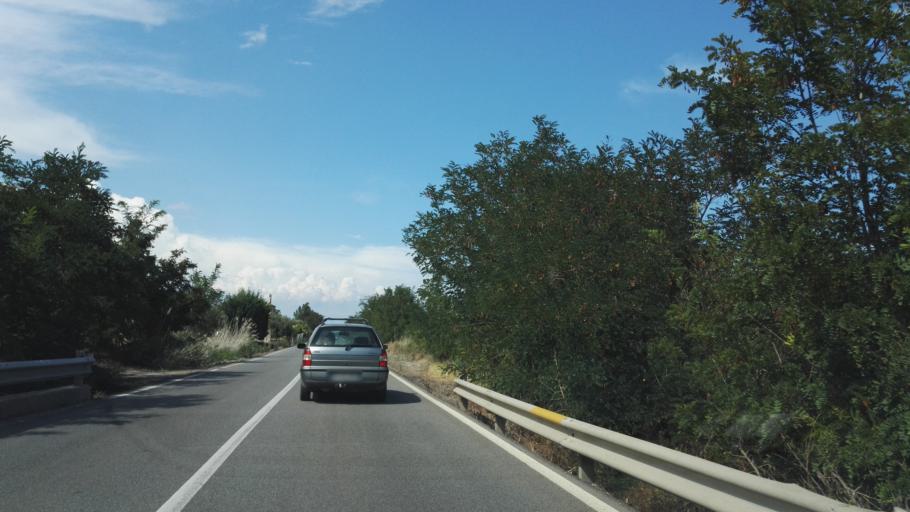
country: IT
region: Calabria
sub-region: Provincia di Catanzaro
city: Santa Caterina dello Ionio Marina
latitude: 38.5517
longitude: 16.5704
